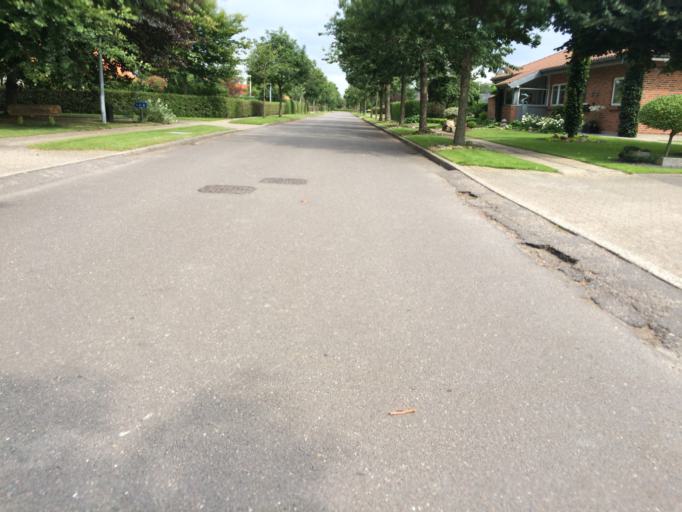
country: DK
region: Central Jutland
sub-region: Holstebro Kommune
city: Ulfborg
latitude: 56.2729
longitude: 8.3067
